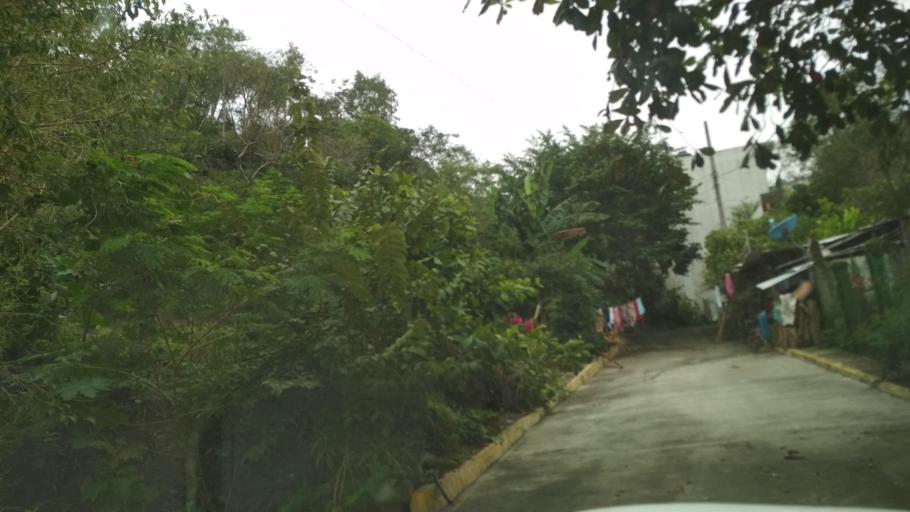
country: MX
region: Veracruz
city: Papantla de Olarte
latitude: 20.4431
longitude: -97.3093
